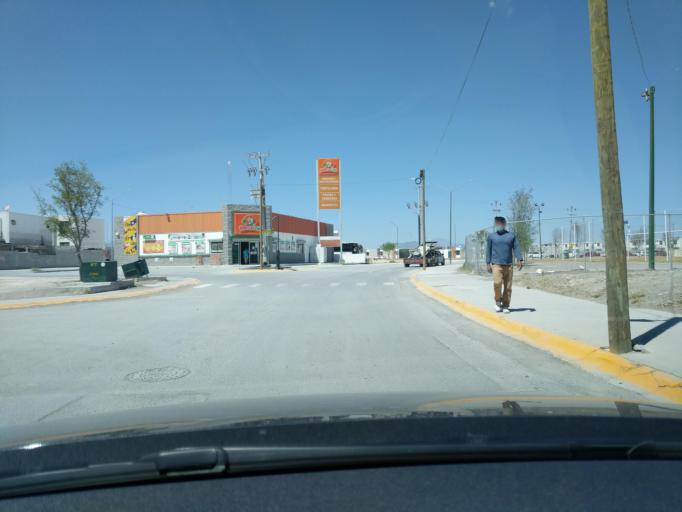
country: MX
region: Nuevo Leon
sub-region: Apodaca
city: Artemio Trevino
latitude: 25.8404
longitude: -100.1425
